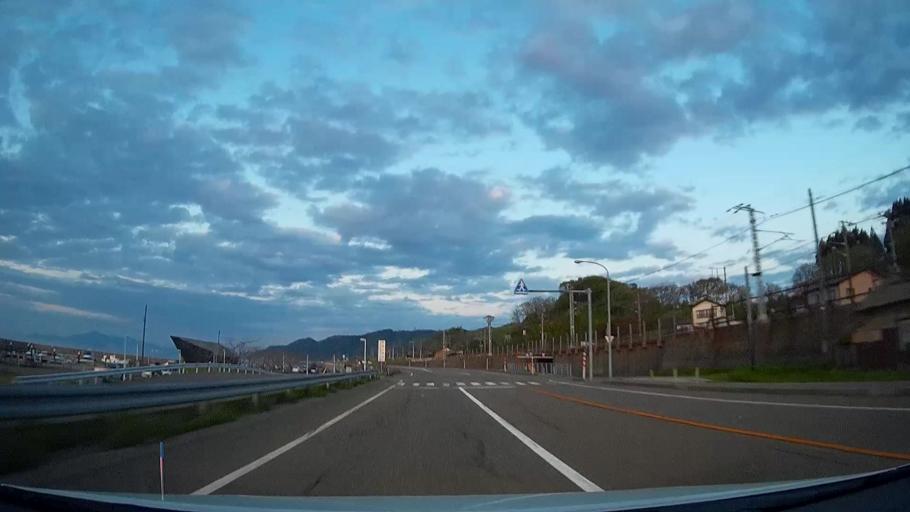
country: JP
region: Niigata
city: Joetsu
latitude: 37.1637
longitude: 138.1401
